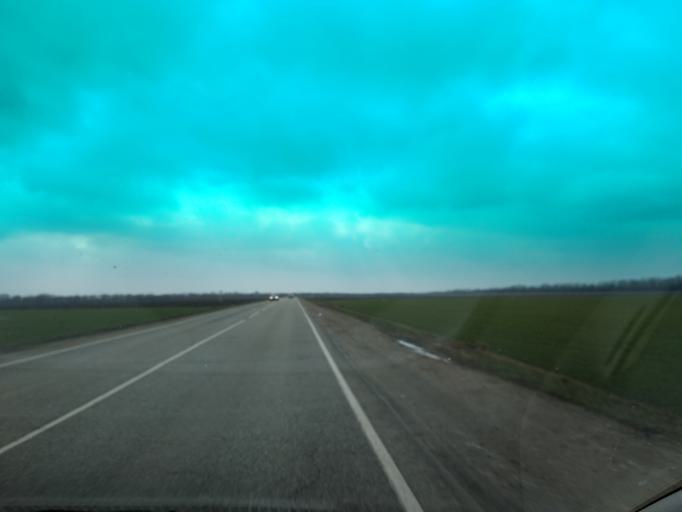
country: RU
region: Krasnodarskiy
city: Novomalorossiyskaya
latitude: 45.7376
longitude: 39.9117
